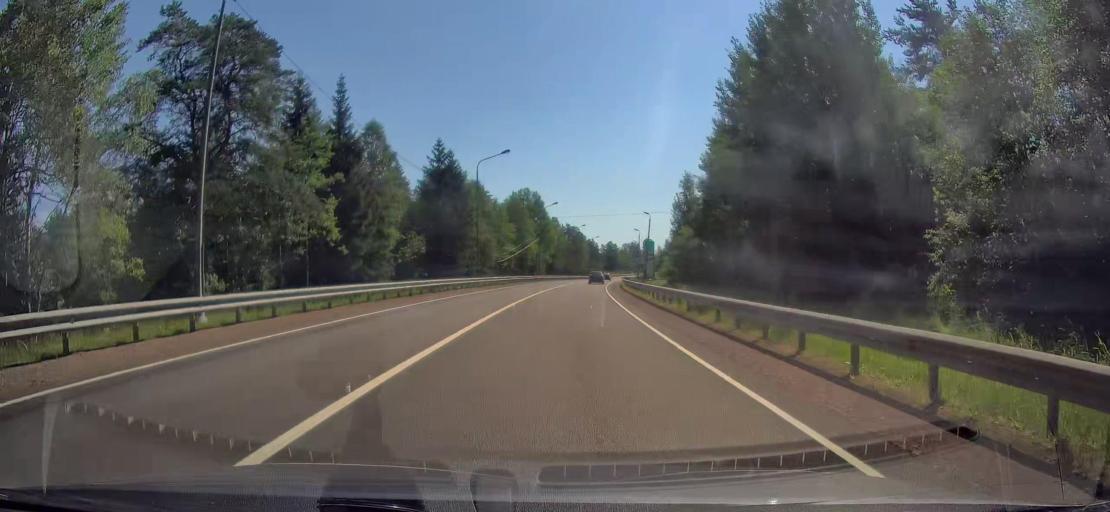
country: RU
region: Leningrad
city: Yefimovskiy
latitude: 59.3466
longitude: 34.8670
